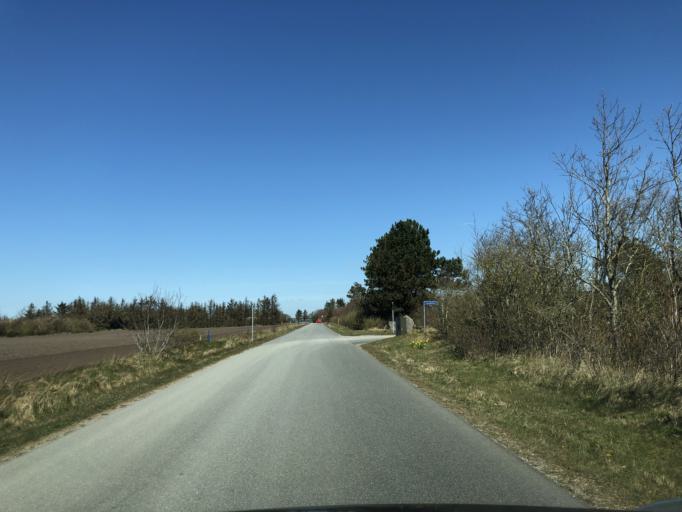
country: DK
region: Central Jutland
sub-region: Holstebro Kommune
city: Ulfborg
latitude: 56.3166
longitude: 8.1964
